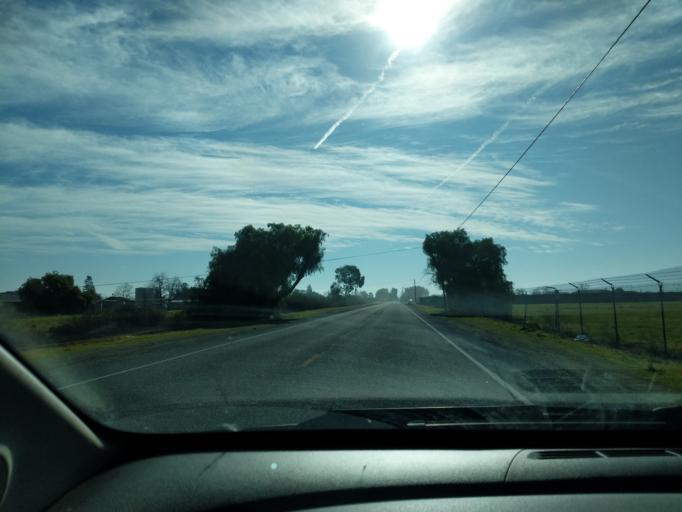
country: US
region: California
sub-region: Santa Clara County
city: San Martin
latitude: 37.0792
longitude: -121.6032
